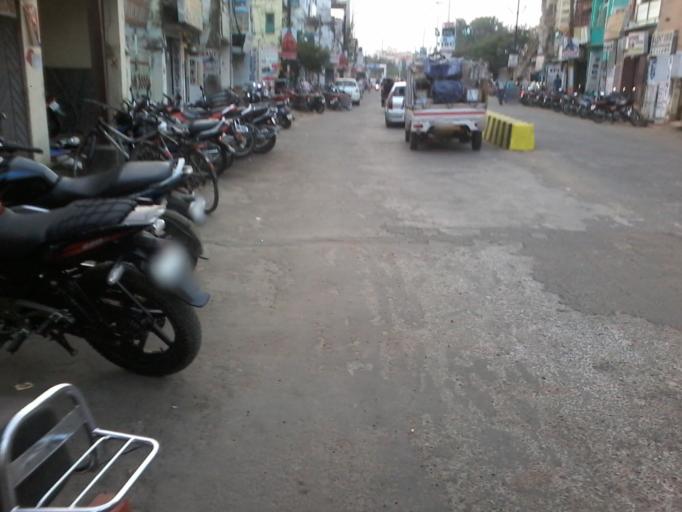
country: IN
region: Odisha
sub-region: Ganjam
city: Brahmapur
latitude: 19.3089
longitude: 84.7937
